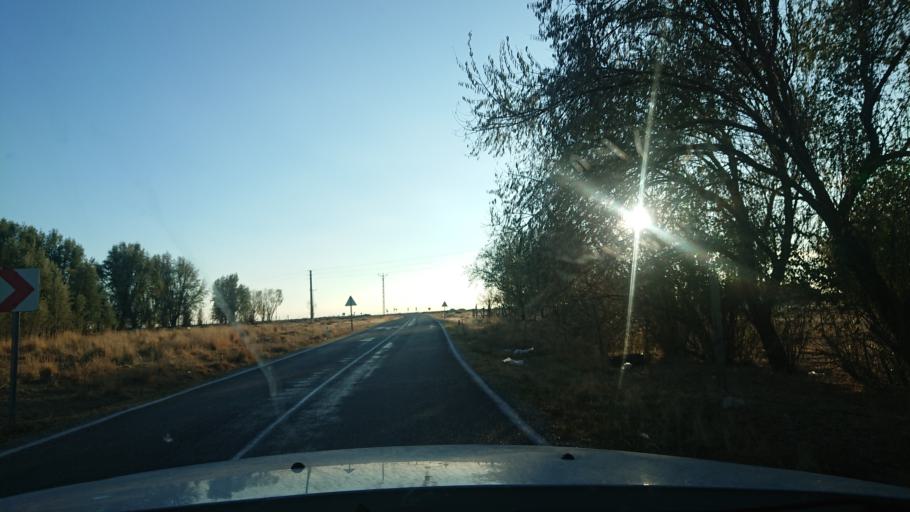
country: TR
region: Aksaray
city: Eskil
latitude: 38.5276
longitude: 33.2074
